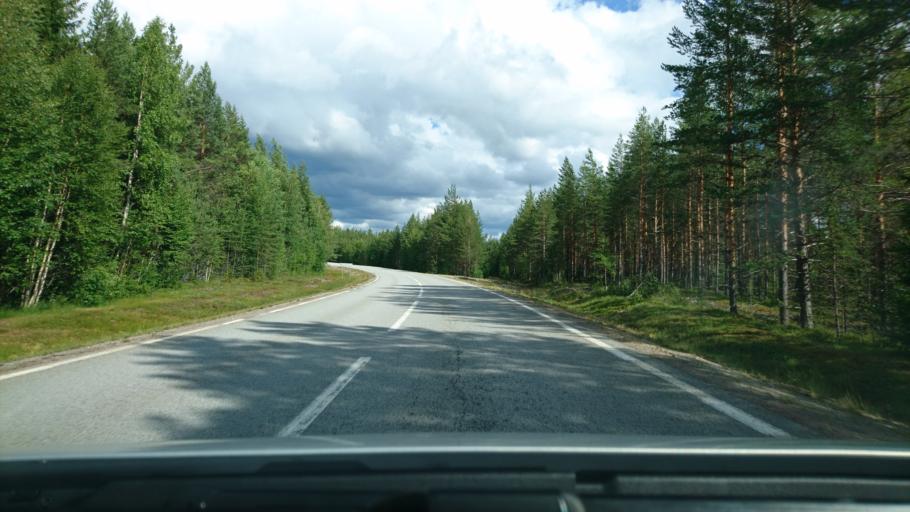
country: SE
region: Vaesterbotten
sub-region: Asele Kommun
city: Asele
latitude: 63.7864
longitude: 17.0710
